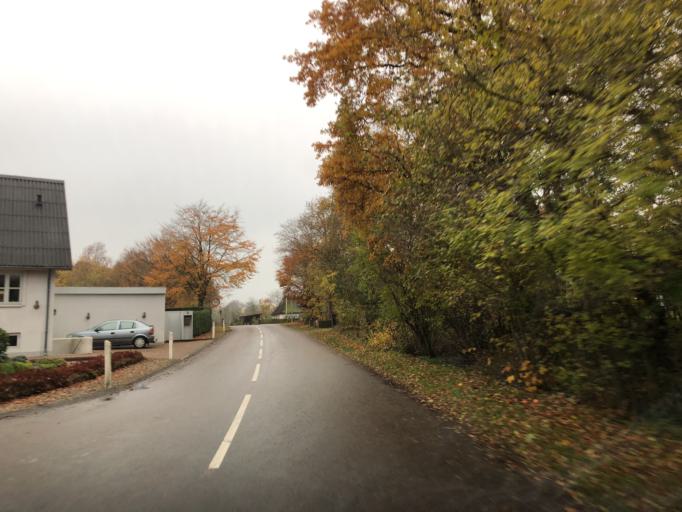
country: DK
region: Central Jutland
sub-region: Herning Kommune
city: Avlum
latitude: 56.2475
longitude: 8.8789
